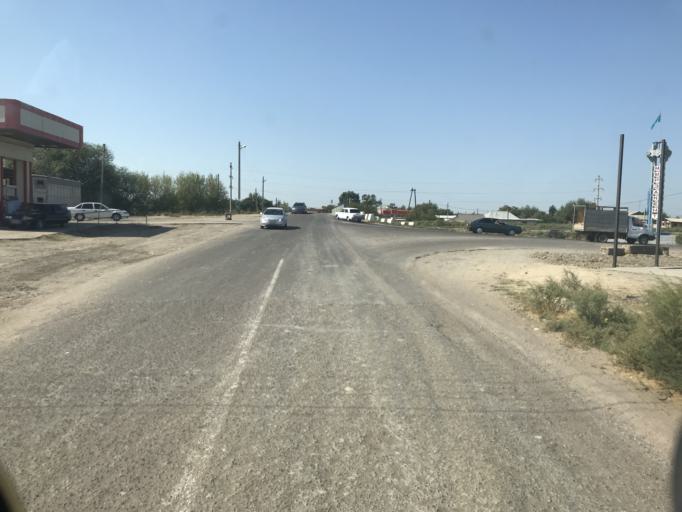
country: KZ
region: Ongtustik Qazaqstan
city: Myrzakent
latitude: 40.6699
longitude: 68.5517
